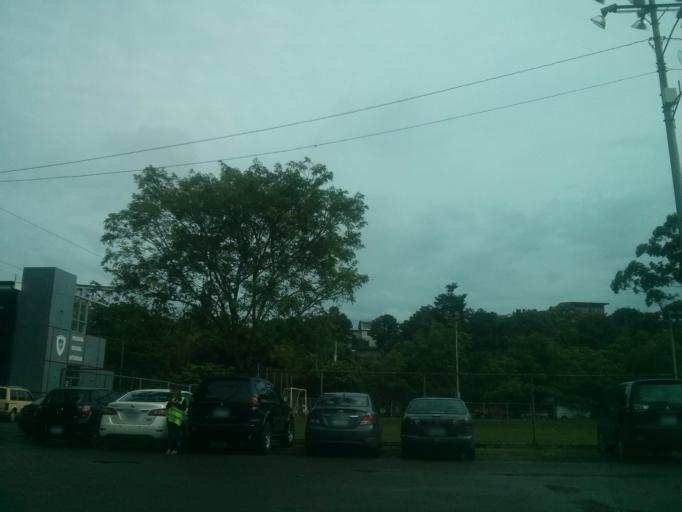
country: CR
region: San Jose
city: Calle Blancos
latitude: 9.9398
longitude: -84.0691
